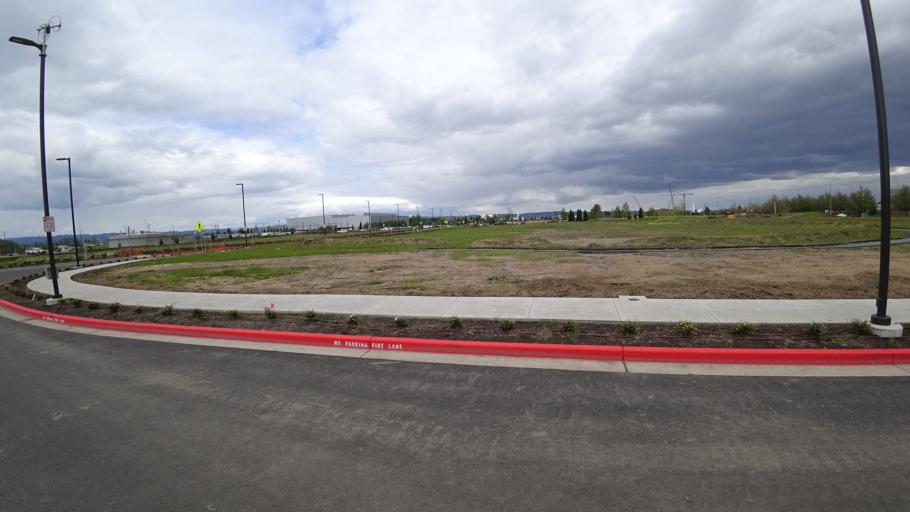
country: US
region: Oregon
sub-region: Washington County
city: Rockcreek
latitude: 45.5518
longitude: -122.9333
